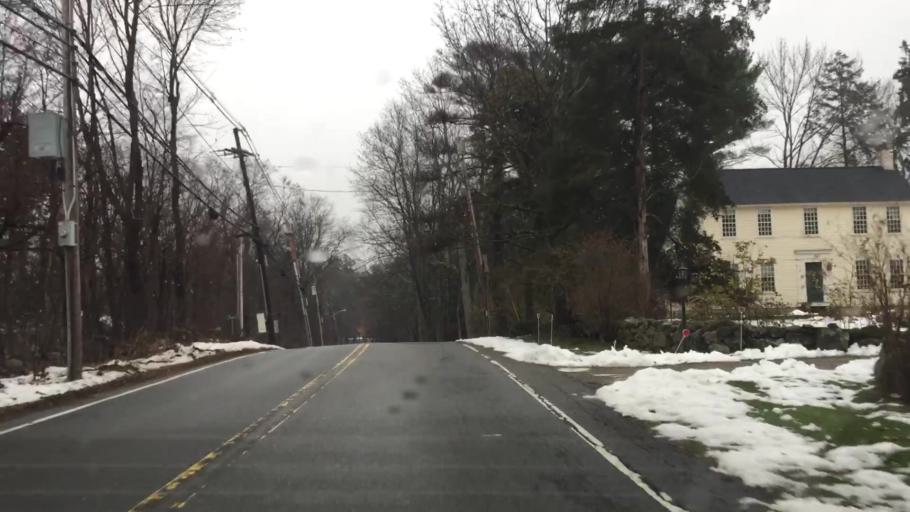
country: US
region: Massachusetts
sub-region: Essex County
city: North Andover
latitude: 42.6951
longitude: -71.0877
